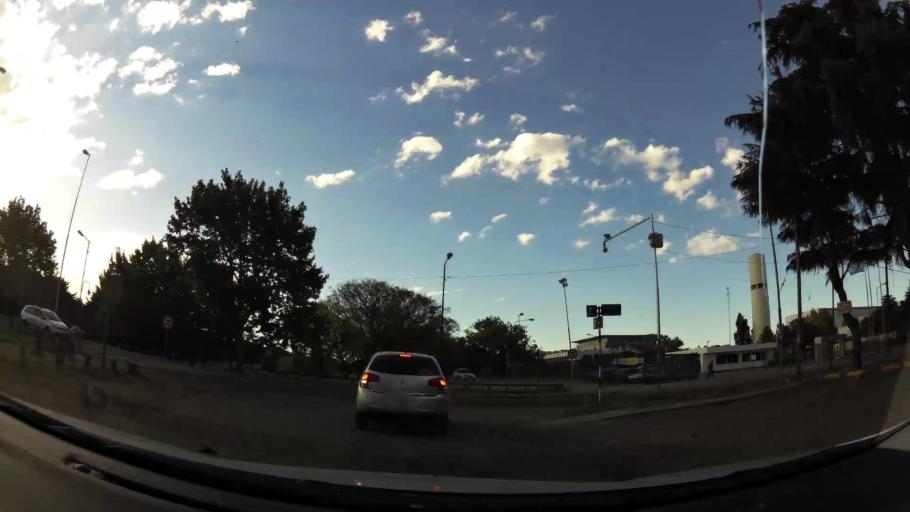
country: AR
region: Buenos Aires
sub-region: Partido de Tigre
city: Tigre
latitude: -34.4709
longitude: -58.5651
